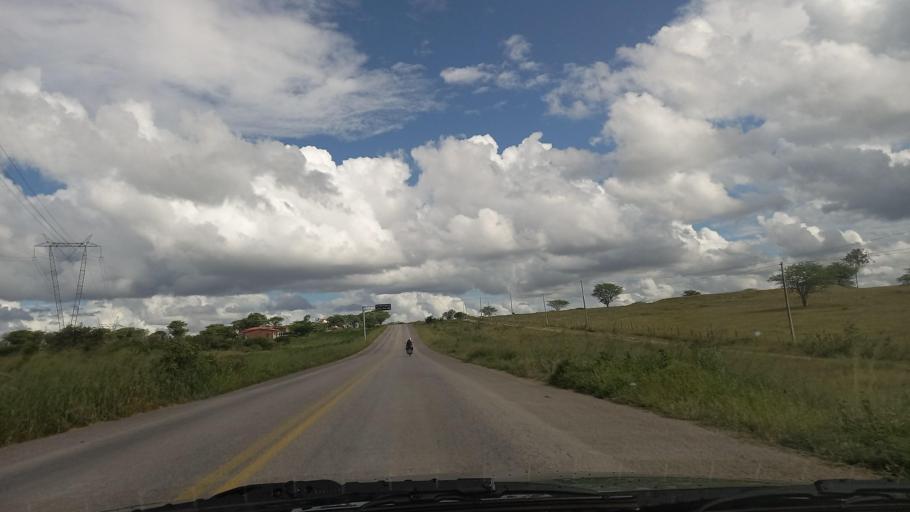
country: BR
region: Pernambuco
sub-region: Lajedo
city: Lajedo
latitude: -8.6034
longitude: -36.2930
